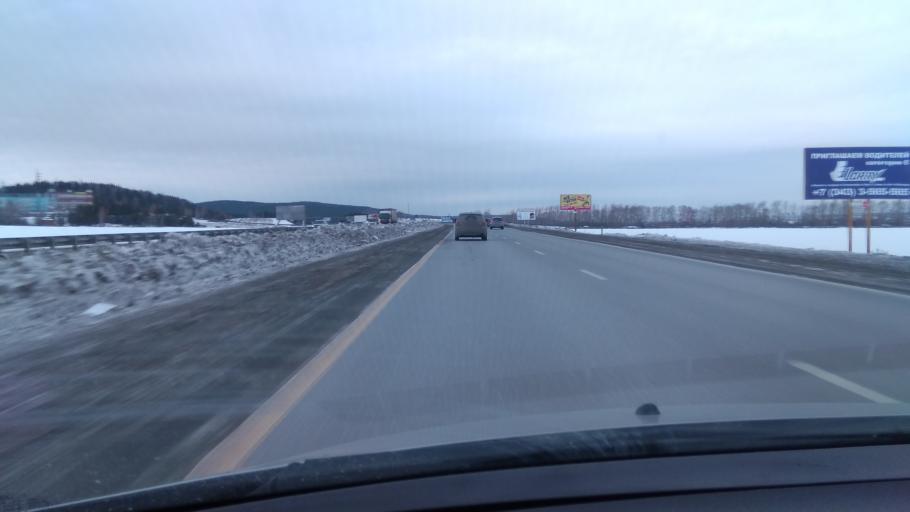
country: RU
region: Sverdlovsk
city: Aramil
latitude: 56.6890
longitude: 60.7667
